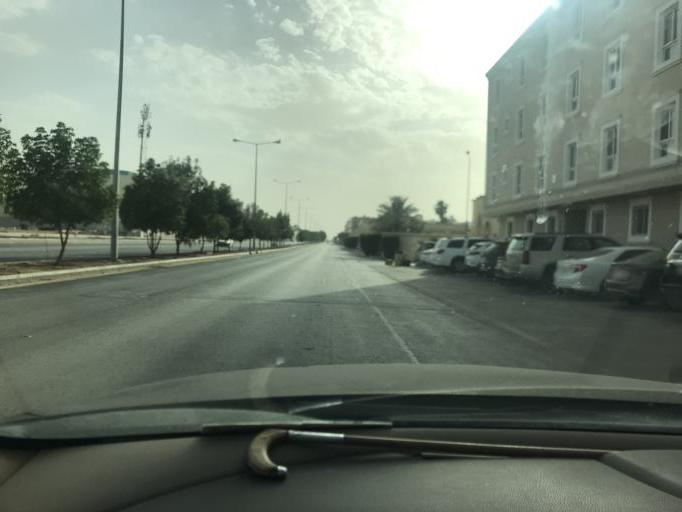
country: SA
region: Ar Riyad
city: Riyadh
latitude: 24.7806
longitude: 46.7152
